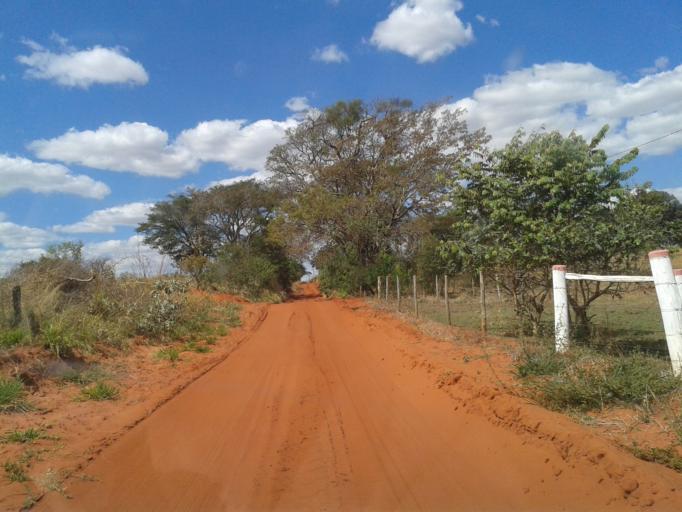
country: BR
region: Minas Gerais
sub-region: Centralina
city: Centralina
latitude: -18.7770
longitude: -49.0878
